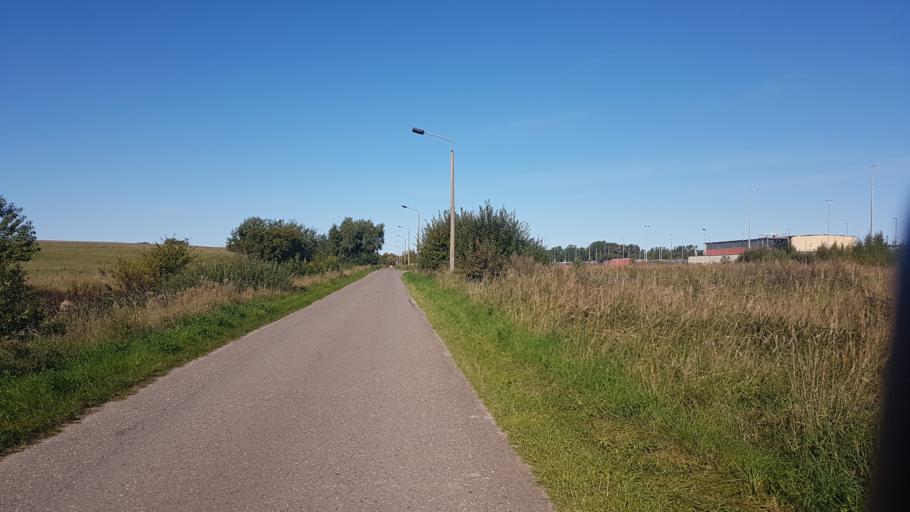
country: DE
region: Mecklenburg-Vorpommern
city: Sagard
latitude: 54.4976
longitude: 13.5460
